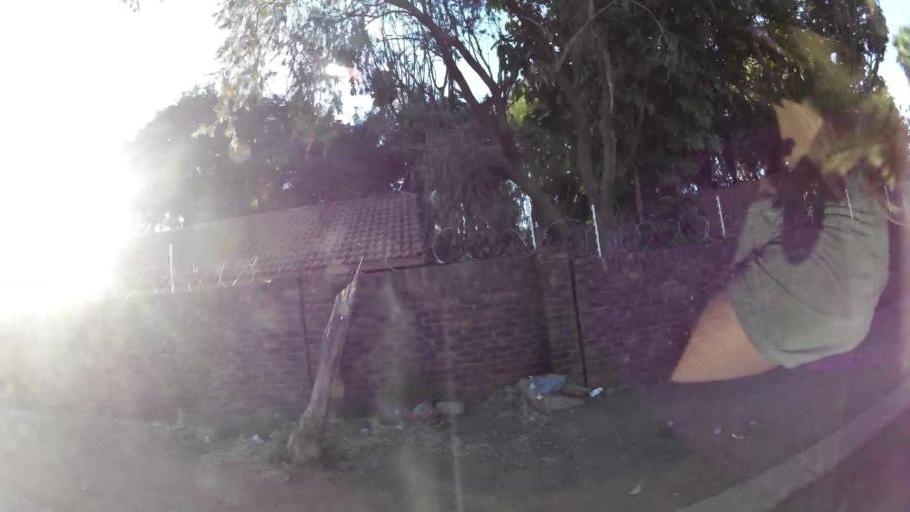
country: ZA
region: North-West
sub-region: Bojanala Platinum District Municipality
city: Rustenburg
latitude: -25.6445
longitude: 27.2254
